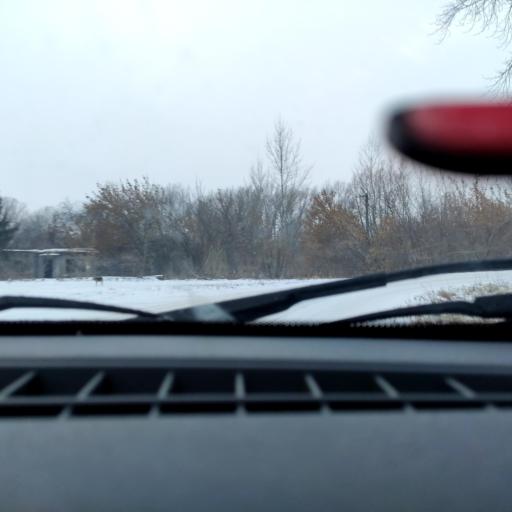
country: RU
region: Bashkortostan
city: Blagoveshchensk
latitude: 54.9057
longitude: 56.0101
